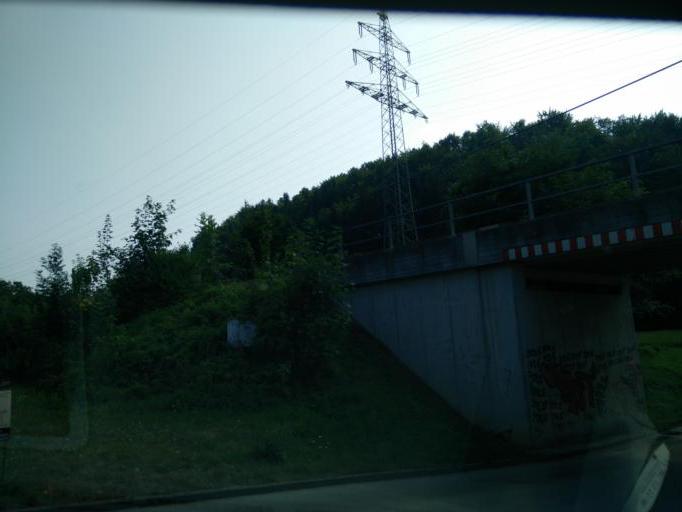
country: DE
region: Baden-Wuerttemberg
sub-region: Tuebingen Region
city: Dusslingen
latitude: 48.4882
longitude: 9.0661
